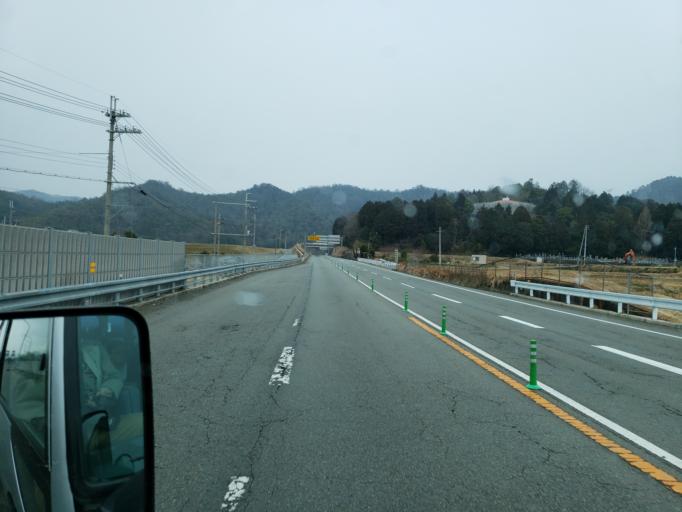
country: JP
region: Hyogo
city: Himeji
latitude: 34.9580
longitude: 134.7700
